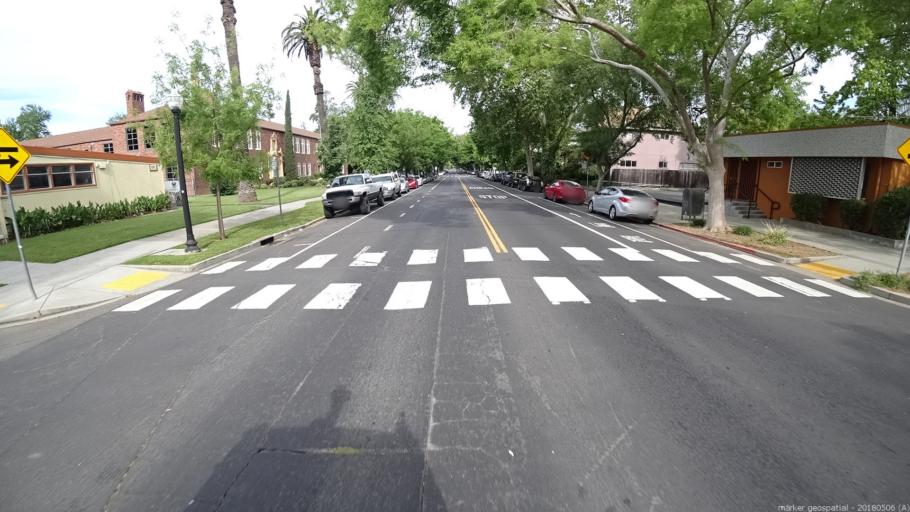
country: US
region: California
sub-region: Sacramento County
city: Sacramento
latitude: 38.5705
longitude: -121.4753
